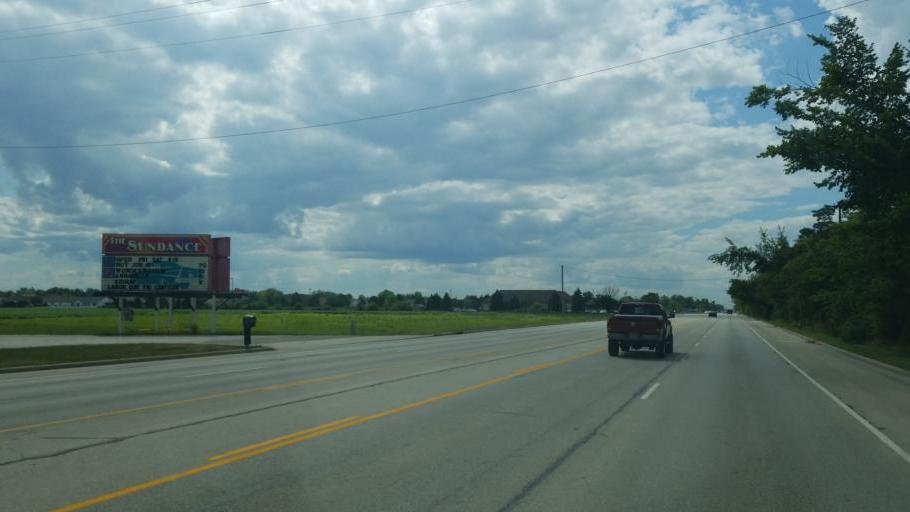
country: US
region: Ohio
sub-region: Wood County
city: Northwood
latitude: 41.6376
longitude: -83.4399
